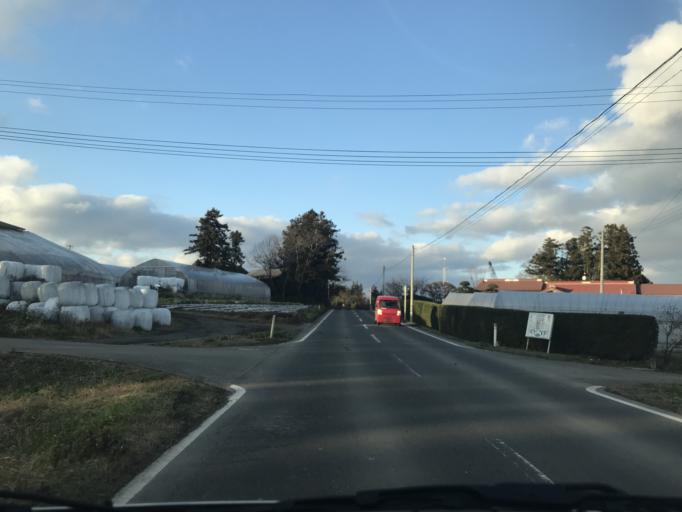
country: JP
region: Miyagi
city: Kogota
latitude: 38.6344
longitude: 141.0697
